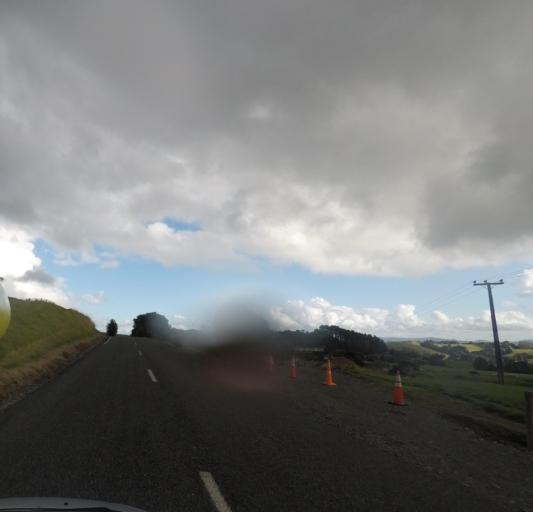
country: NZ
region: Auckland
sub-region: Auckland
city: Warkworth
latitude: -36.3709
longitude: 174.7650
